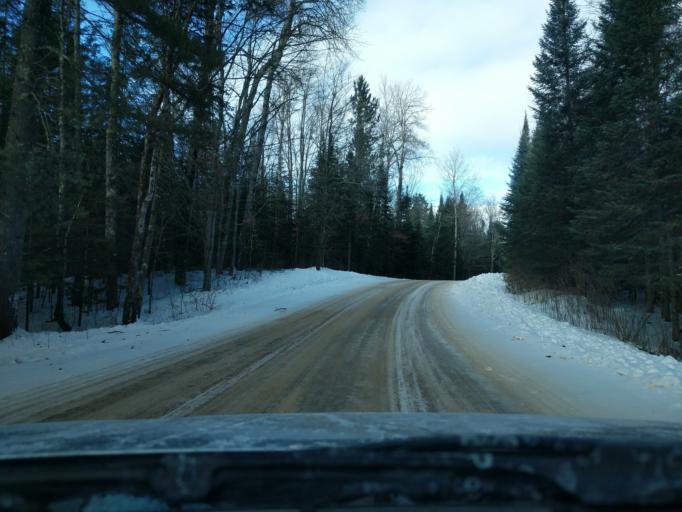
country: US
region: Wisconsin
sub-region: Vilas County
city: Eagle River
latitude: 45.8050
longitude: -89.0706
